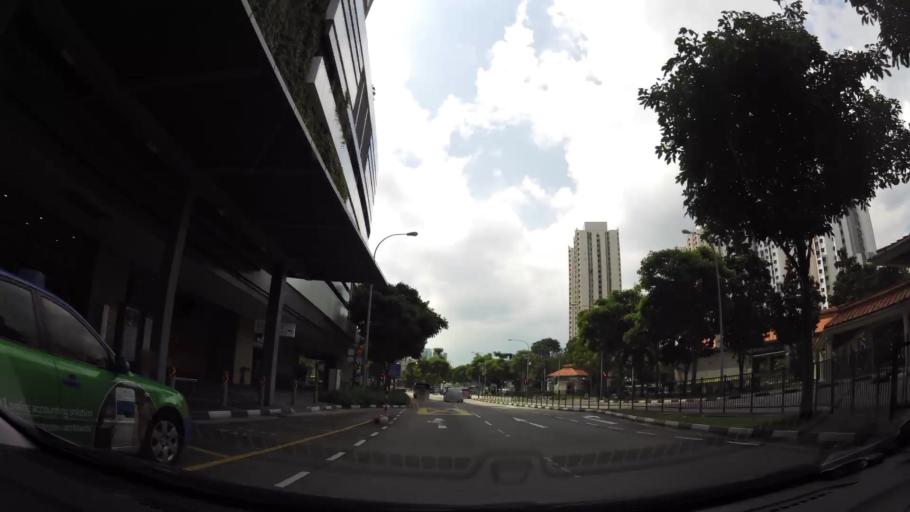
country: SG
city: Singapore
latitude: 1.3124
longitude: 103.8534
